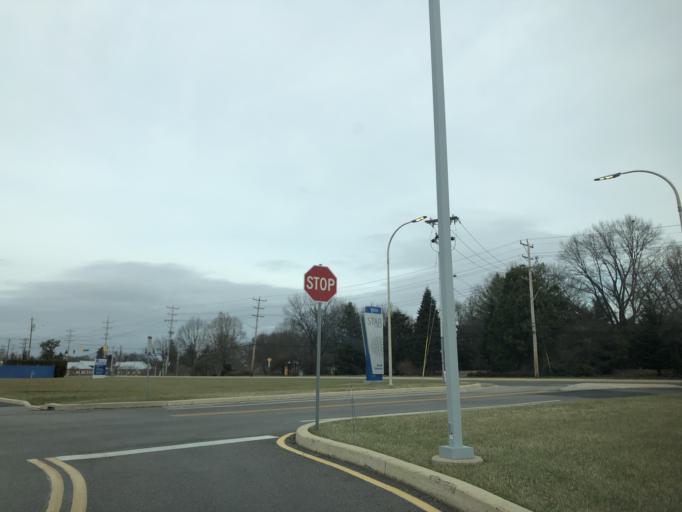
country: US
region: Delaware
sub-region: New Castle County
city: Newark
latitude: 39.6657
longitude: -75.7533
